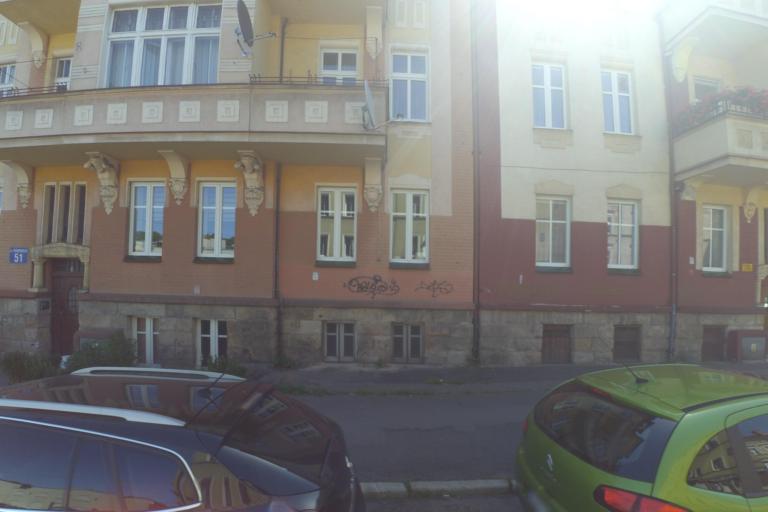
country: PL
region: Lower Silesian Voivodeship
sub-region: Powiat walbrzyski
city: Walbrzych
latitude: 50.7615
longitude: 16.2840
